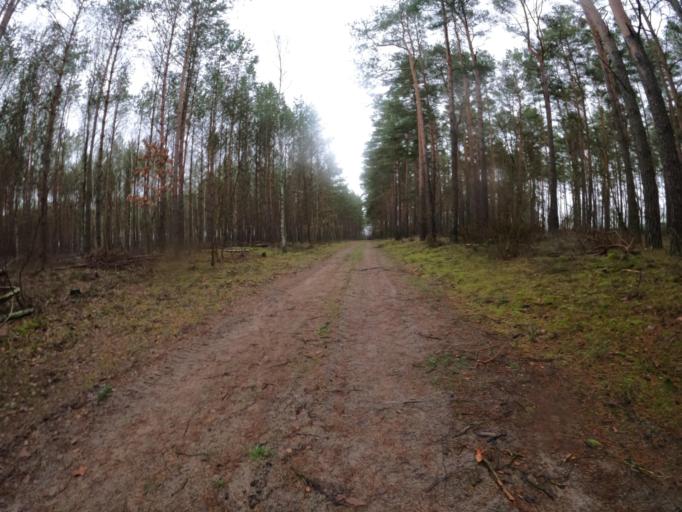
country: PL
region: West Pomeranian Voivodeship
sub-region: Powiat mysliborski
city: Debno
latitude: 52.7720
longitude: 14.7571
